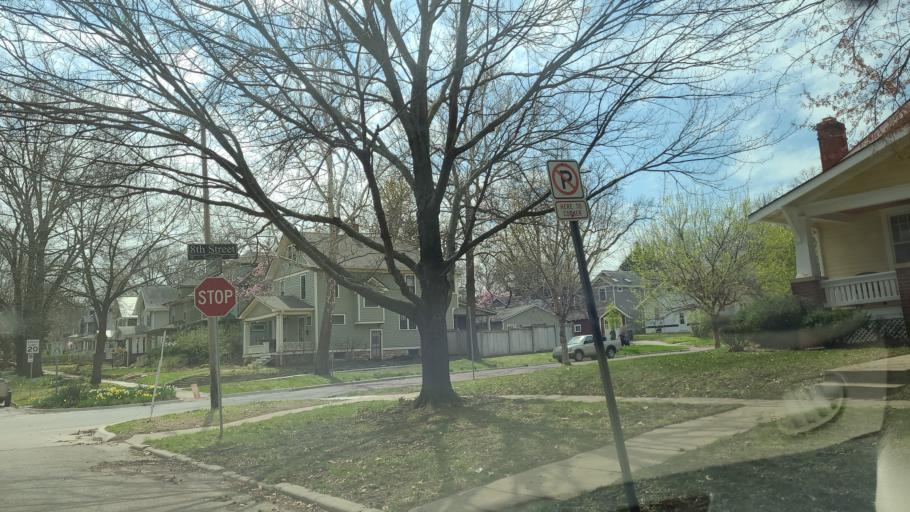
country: US
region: Kansas
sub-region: Douglas County
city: Lawrence
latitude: 38.9696
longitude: -95.2487
